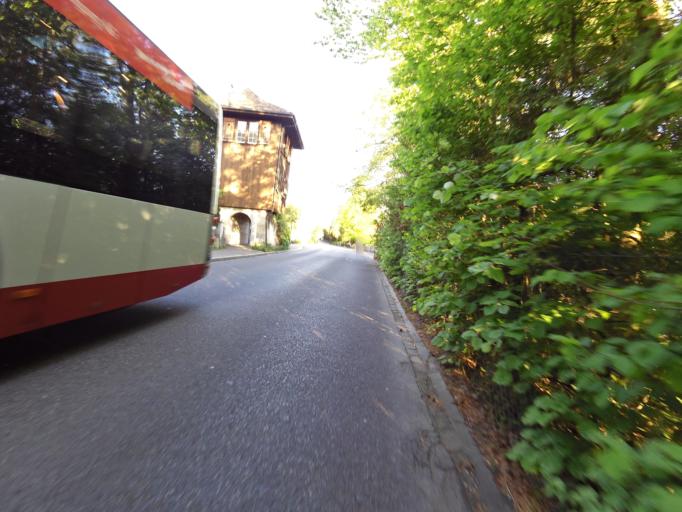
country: CH
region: Zurich
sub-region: Bezirk Winterthur
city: Stadt Winterthur (Kreis 1) / Lind
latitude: 47.5030
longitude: 8.7422
